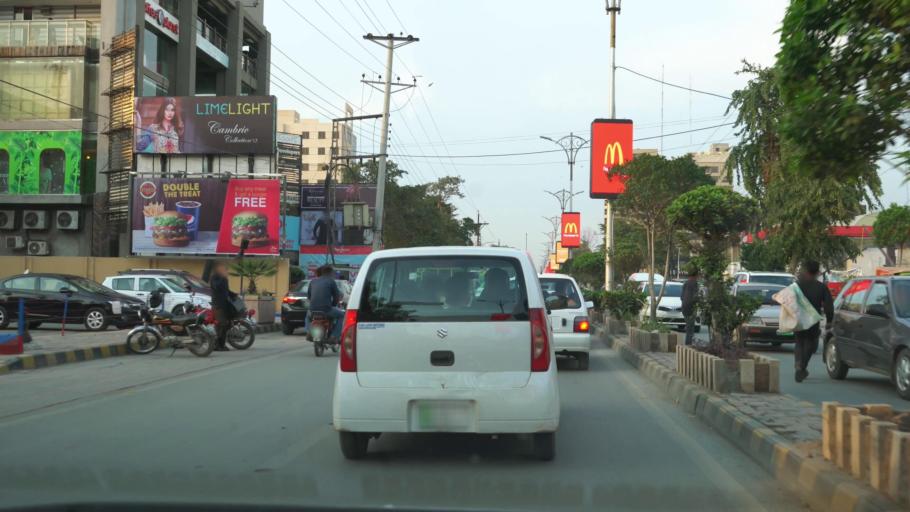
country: PK
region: Punjab
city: Lahore
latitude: 31.5092
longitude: 74.3504
